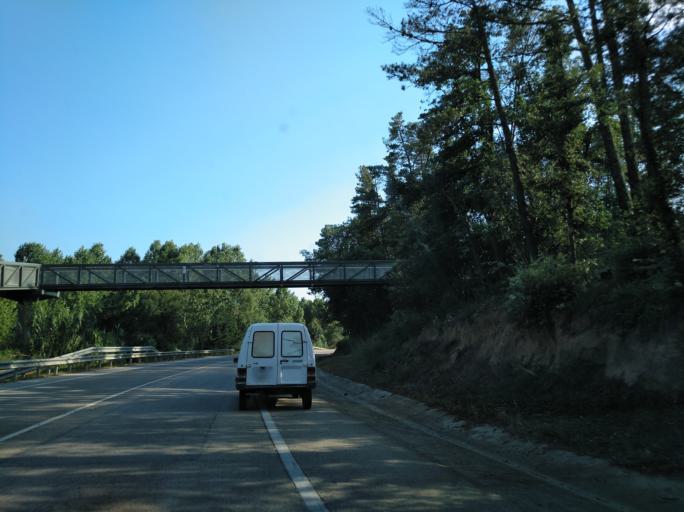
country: ES
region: Catalonia
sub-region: Provincia de Girona
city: Santa Coloma de Farners
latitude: 41.8632
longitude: 2.6906
